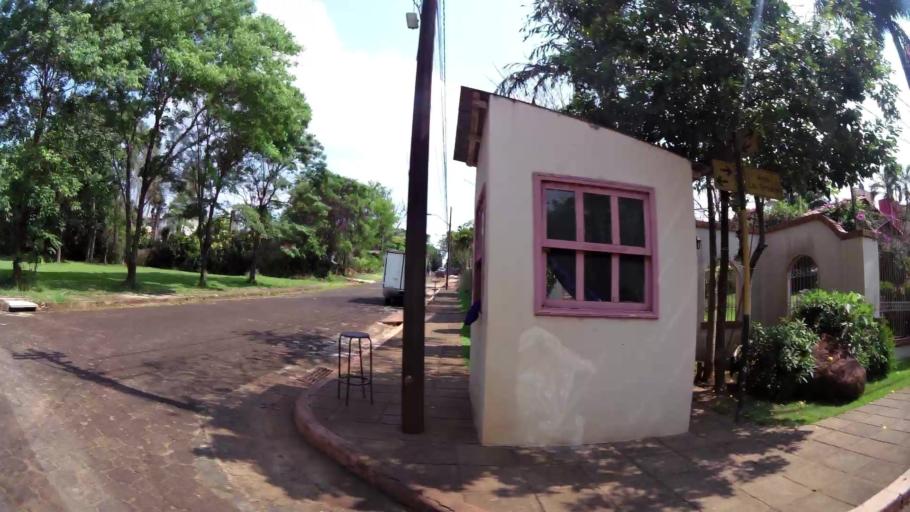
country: PY
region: Alto Parana
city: Ciudad del Este
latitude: -25.5159
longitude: -54.6298
